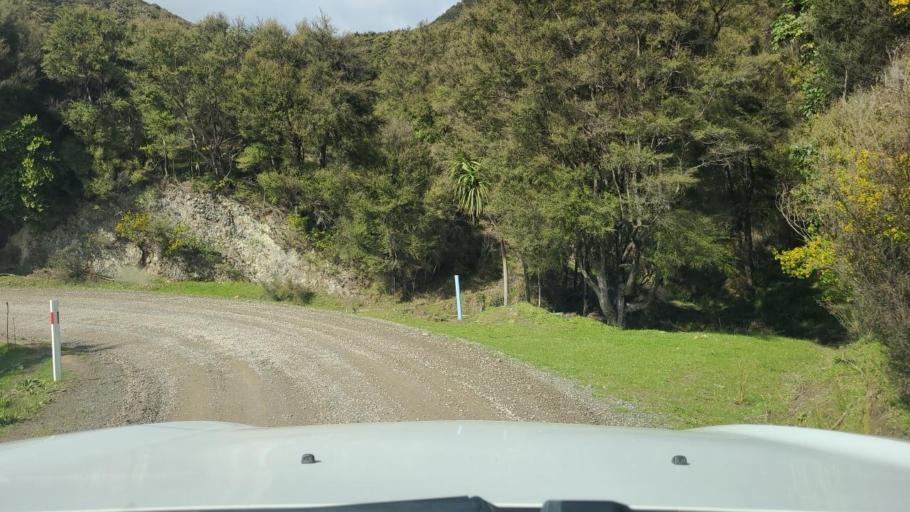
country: NZ
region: Wellington
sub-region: South Wairarapa District
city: Waipawa
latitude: -41.3515
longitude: 175.6903
